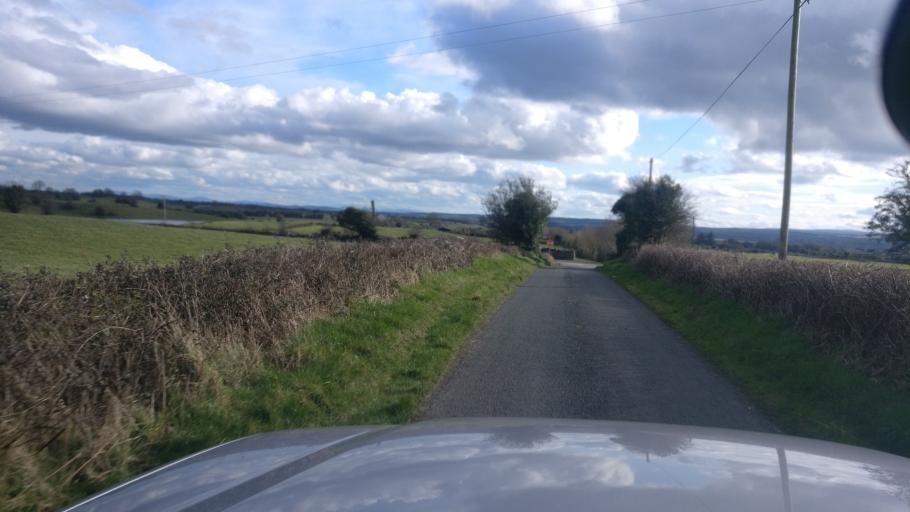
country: IE
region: Connaught
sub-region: County Galway
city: Loughrea
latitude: 53.1722
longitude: -8.4267
